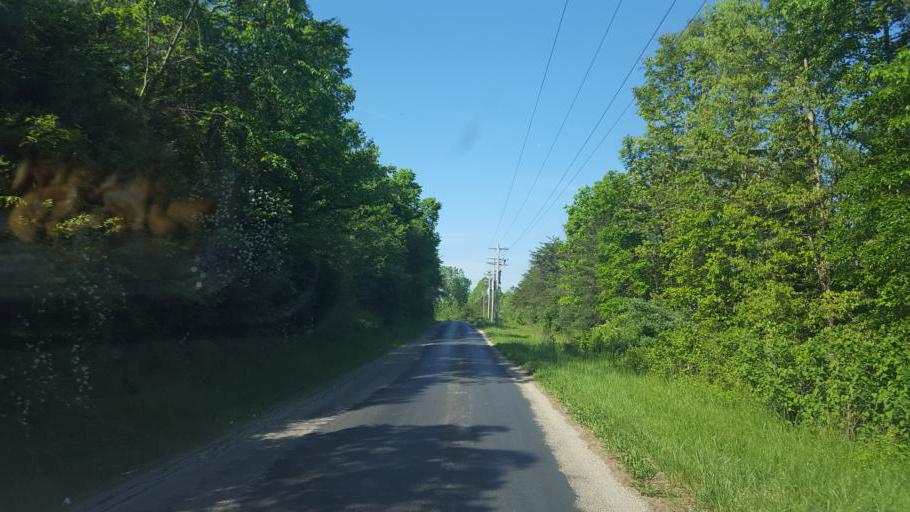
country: US
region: Ohio
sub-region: Jackson County
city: Oak Hill
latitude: 38.9849
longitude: -82.5084
